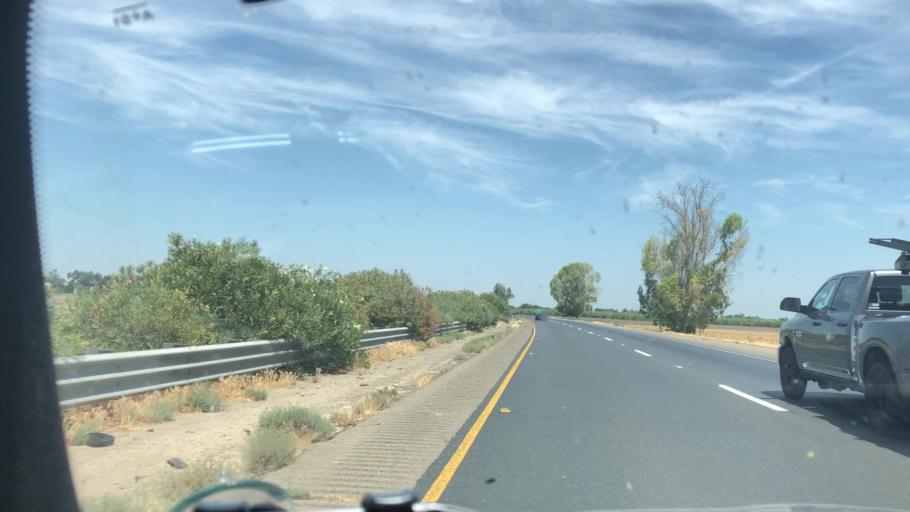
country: US
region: California
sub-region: Tulare County
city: Tipton
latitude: 36.1324
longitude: -119.3256
